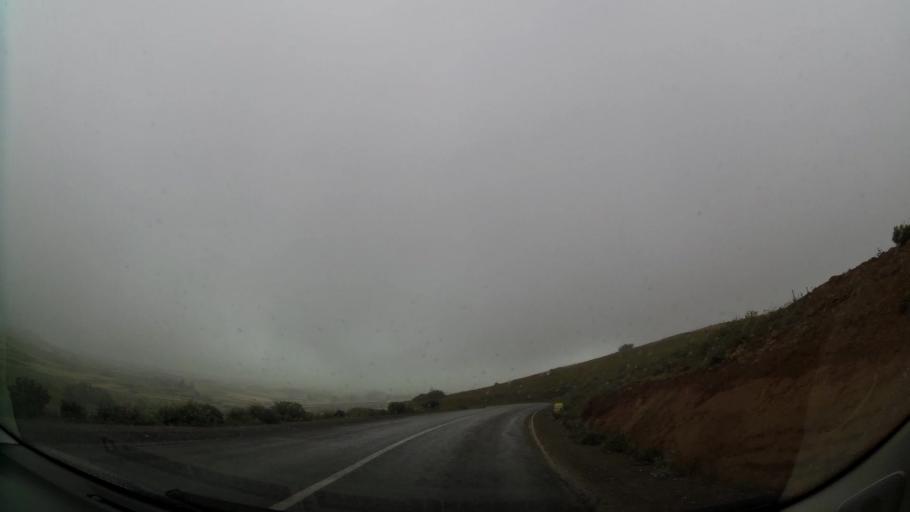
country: MA
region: Oriental
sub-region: Nador
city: Boudinar
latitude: 35.1380
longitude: -3.6046
